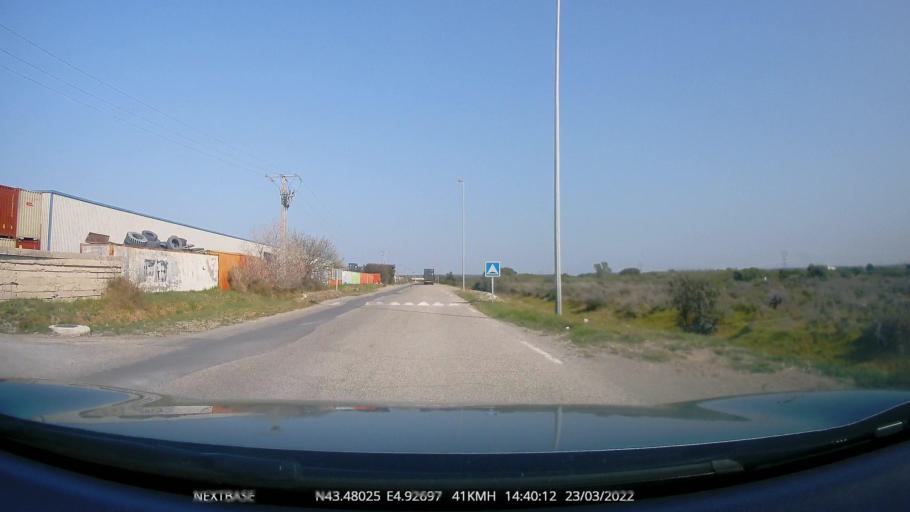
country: FR
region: Provence-Alpes-Cote d'Azur
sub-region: Departement des Bouches-du-Rhone
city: Fos-sur-Mer
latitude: 43.4811
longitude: 4.9274
